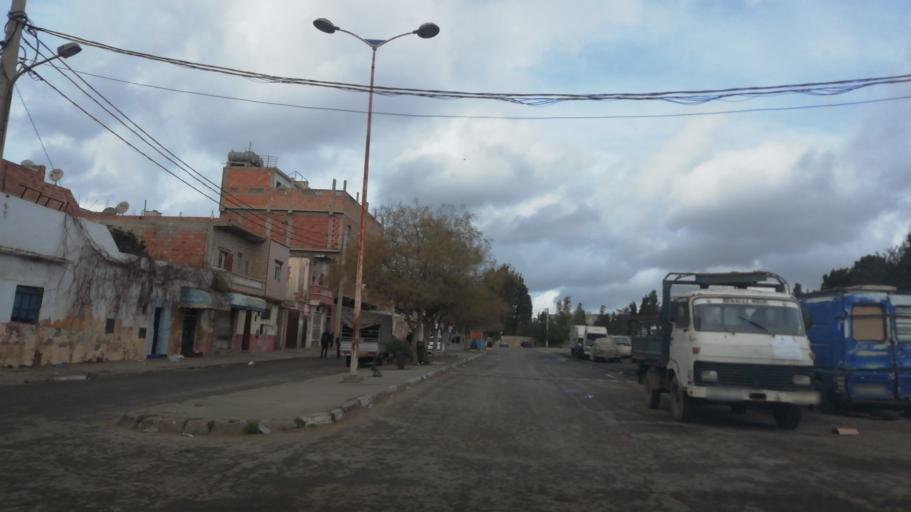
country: DZ
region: Oran
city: Oran
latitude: 35.6877
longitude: -0.6353
